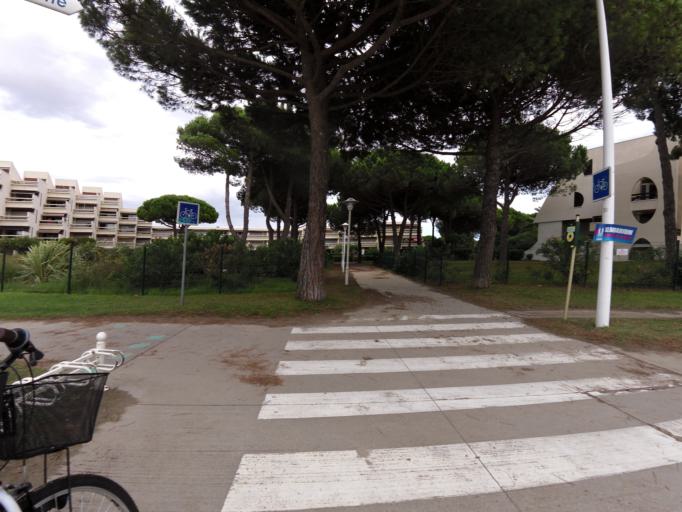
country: FR
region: Languedoc-Roussillon
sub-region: Departement du Gard
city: Le Grau-du-Roi
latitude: 43.5240
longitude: 4.1379
